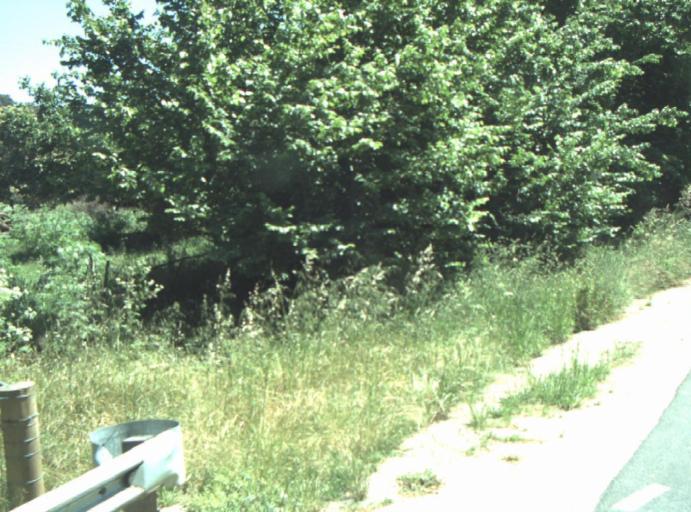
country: AU
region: Victoria
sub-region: Moorabool
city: Bacchus Marsh
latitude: -37.8276
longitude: 144.2894
